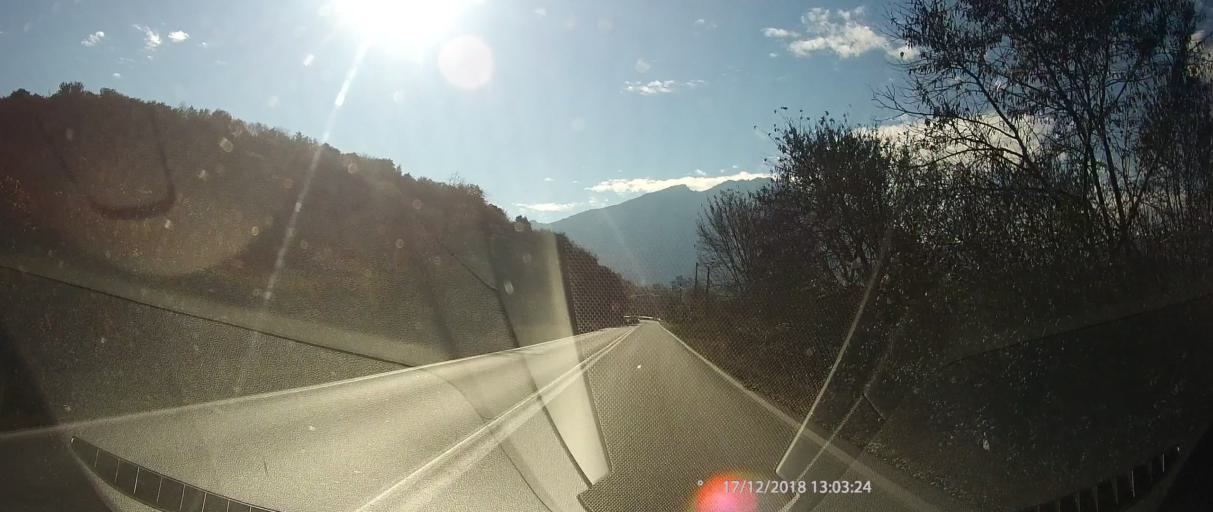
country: GR
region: Thessaly
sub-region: Trikala
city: Kastraki
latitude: 39.7130
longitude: 21.6022
